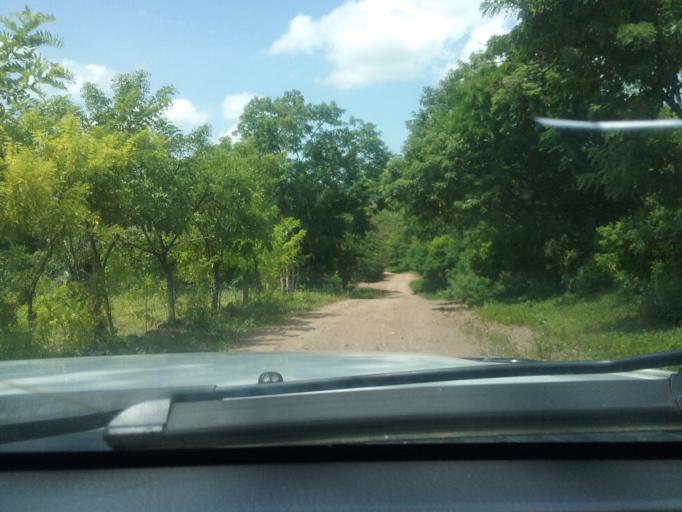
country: NI
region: Matagalpa
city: Terrabona
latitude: 12.6960
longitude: -85.9511
